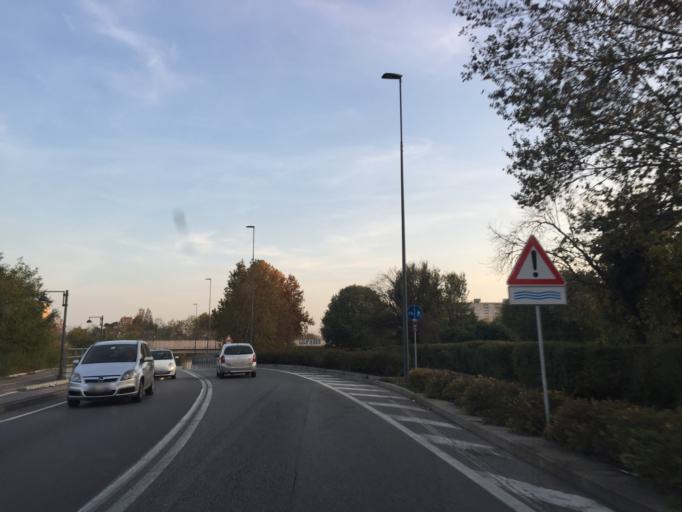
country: IT
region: Lombardy
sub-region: Provincia di Brescia
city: Brescia
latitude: 45.5201
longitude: 10.2468
